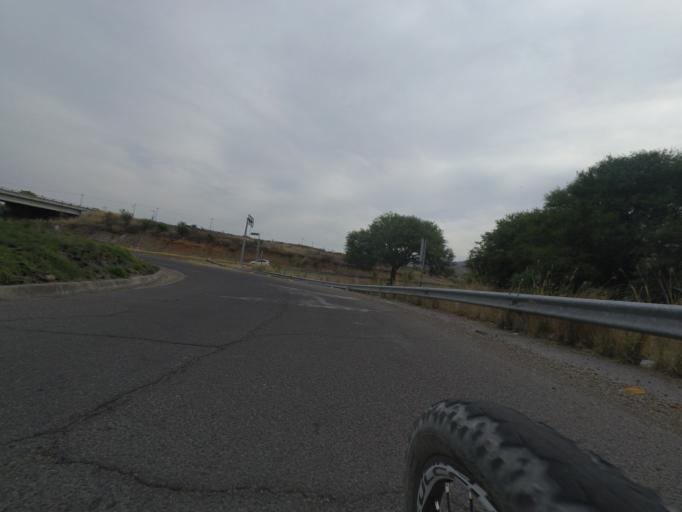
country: MX
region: Aguascalientes
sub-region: Aguascalientes
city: La Loma de los Negritos
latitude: 21.8917
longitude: -102.3991
